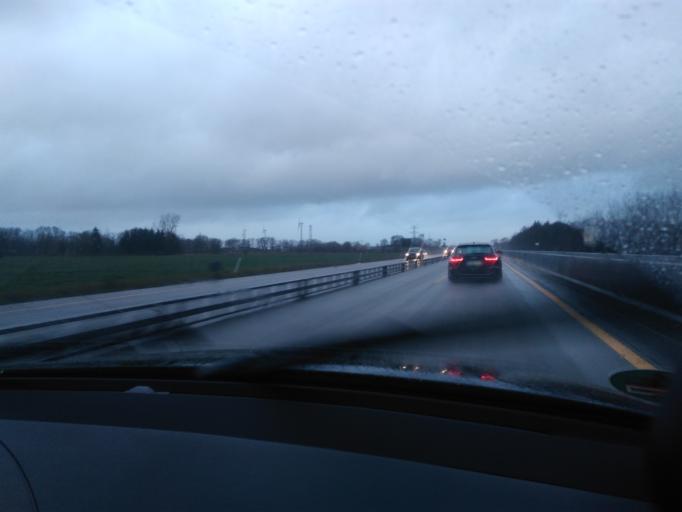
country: DE
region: Schleswig-Holstein
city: Bimohlen
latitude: 53.9476
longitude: 9.9491
